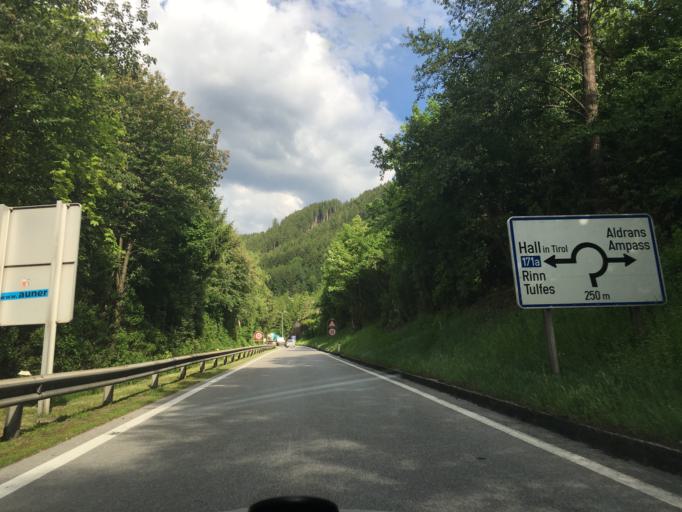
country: AT
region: Tyrol
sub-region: Politischer Bezirk Innsbruck Land
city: Rinn
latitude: 47.2716
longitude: 11.4920
